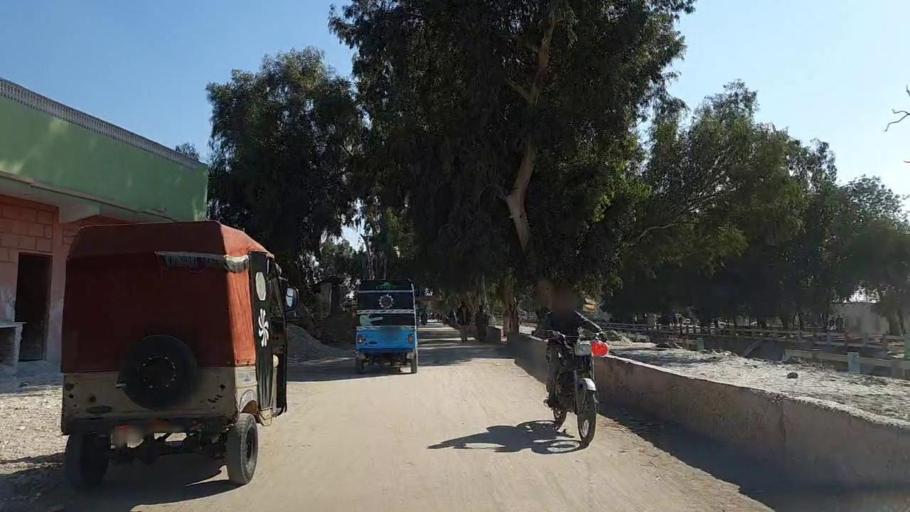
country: PK
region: Sindh
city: Nawabshah
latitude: 26.2537
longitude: 68.4192
